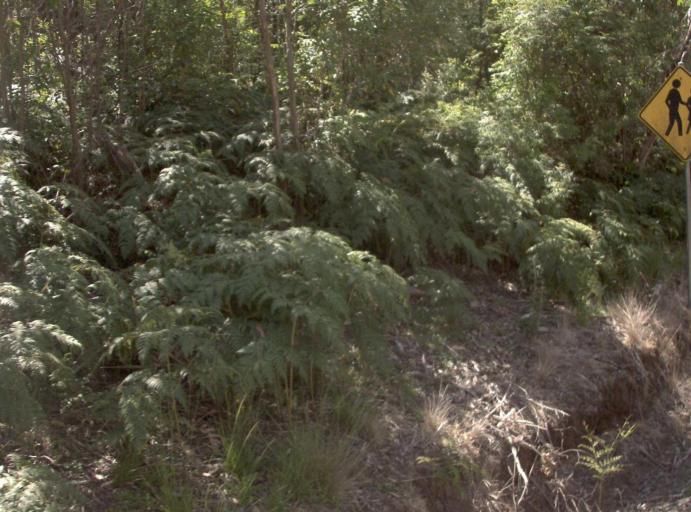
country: AU
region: Victoria
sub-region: Yarra Ranges
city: Millgrove
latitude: -37.5598
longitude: 145.8731
